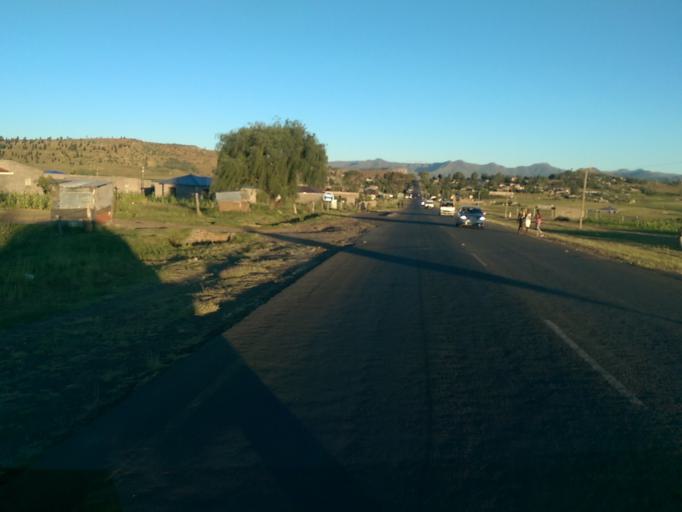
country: LS
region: Maseru
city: Maseru
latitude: -29.4095
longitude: 27.6141
